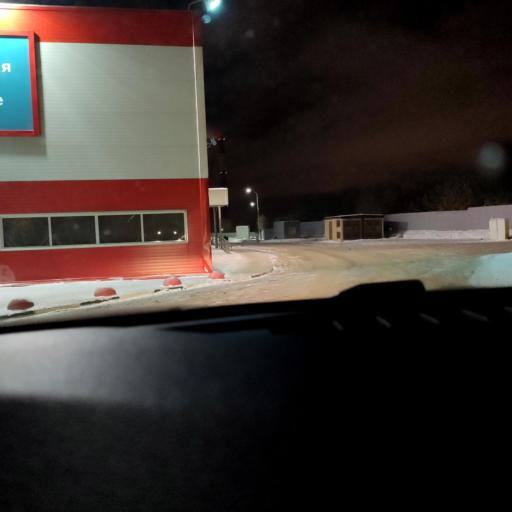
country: RU
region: Samara
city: Samara
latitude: 53.1918
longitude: 50.1664
